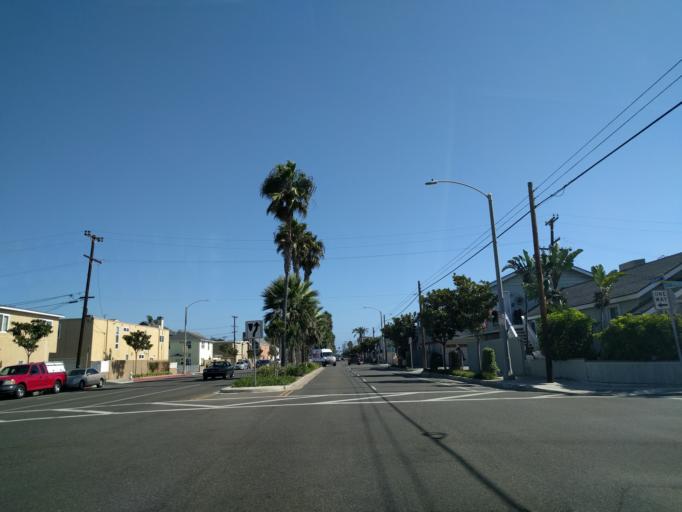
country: US
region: California
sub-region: Orange County
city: Newport Beach
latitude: 33.6198
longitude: -117.9372
